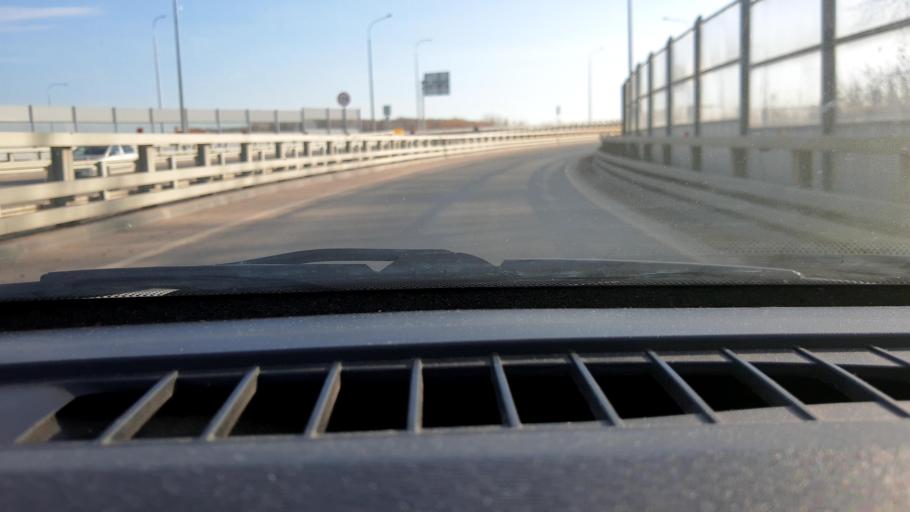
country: RU
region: Nizjnij Novgorod
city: Neklyudovo
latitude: 56.4003
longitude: 43.9896
